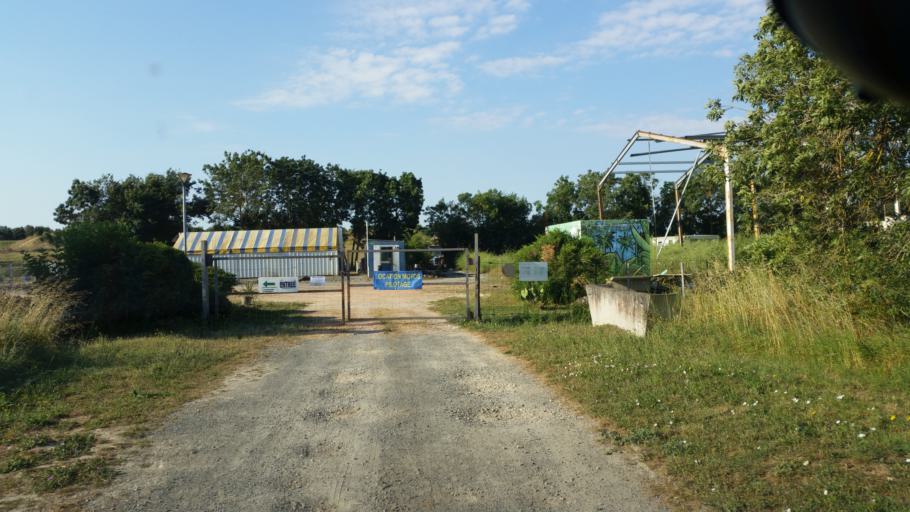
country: FR
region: Poitou-Charentes
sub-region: Departement de la Charente-Maritime
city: Saint-Jean-de-Liversay
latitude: 46.2294
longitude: -0.8850
